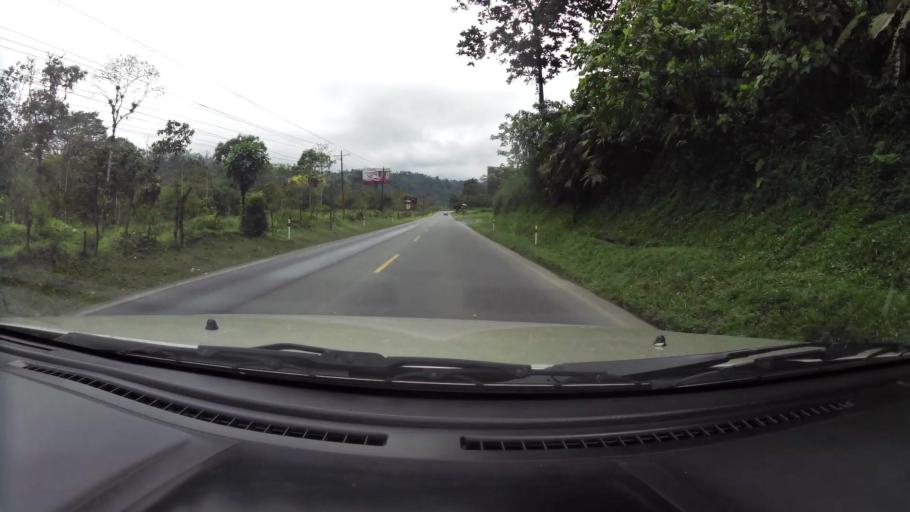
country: EC
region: Santo Domingo de los Tsachilas
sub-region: Canton Santo Domingo de los Colorados
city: Santo Domingo de los Colorados
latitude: -0.2677
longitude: -79.0871
